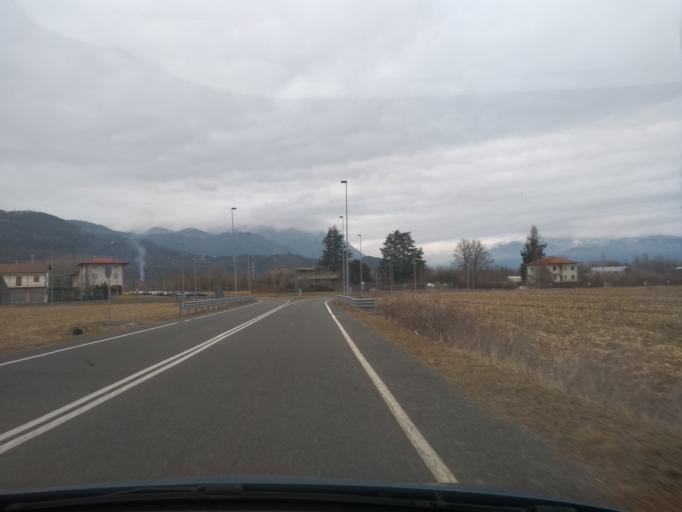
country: IT
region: Piedmont
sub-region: Provincia di Torino
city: Loranze
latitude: 45.4411
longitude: 7.8217
